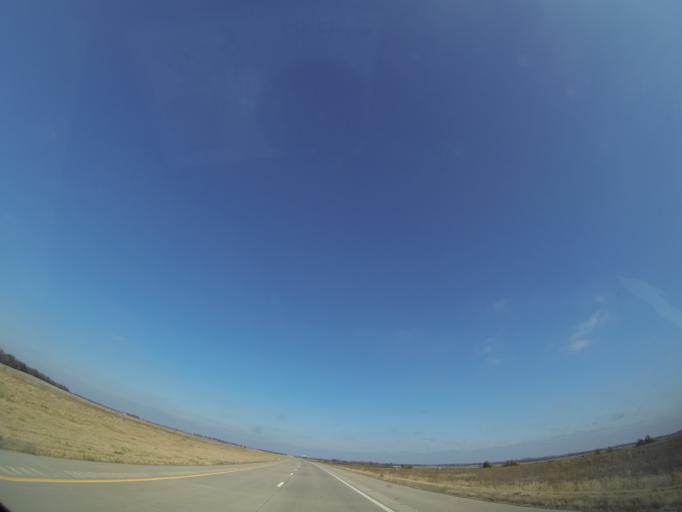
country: US
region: Kansas
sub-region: McPherson County
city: Inman
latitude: 38.2490
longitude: -97.7652
